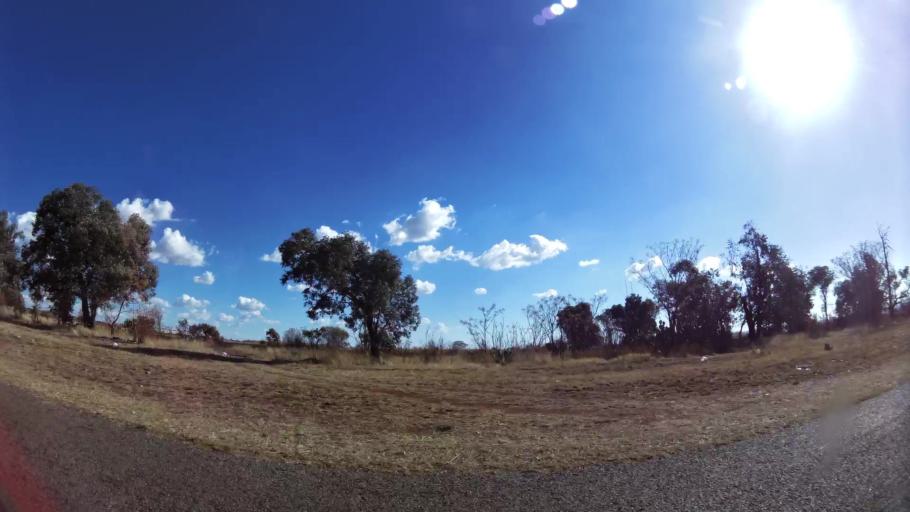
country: ZA
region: Gauteng
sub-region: West Rand District Municipality
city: Carletonville
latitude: -26.3632
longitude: 27.3612
